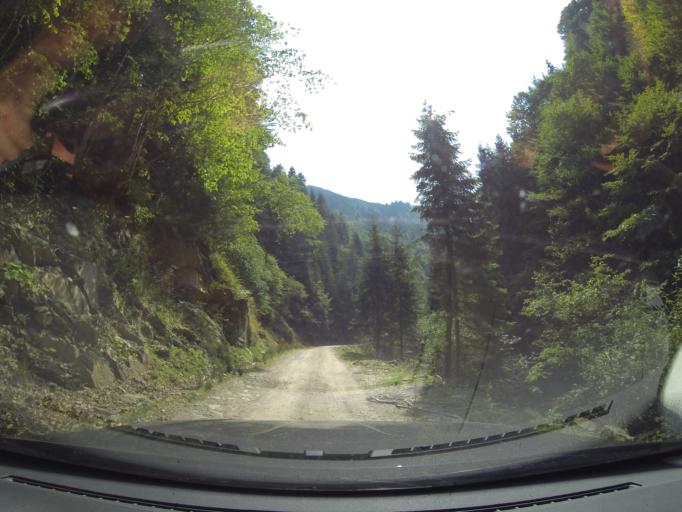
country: RO
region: Arges
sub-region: Comuna Arefu
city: Arefu
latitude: 45.5053
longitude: 24.6596
